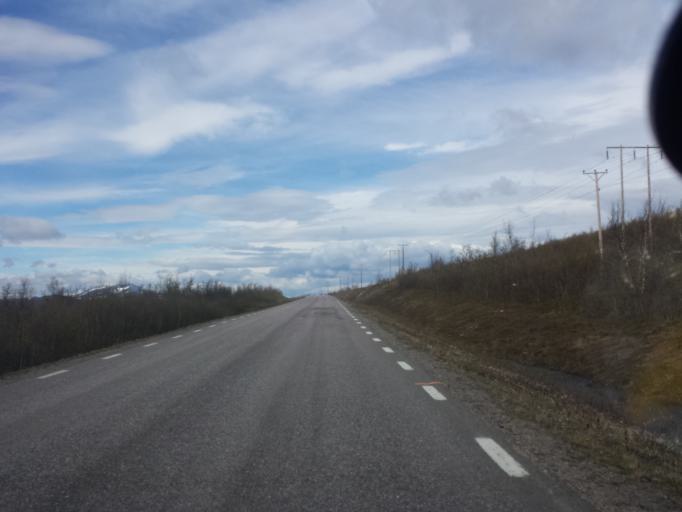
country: SE
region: Norrbotten
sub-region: Kiruna Kommun
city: Kiruna
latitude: 68.0452
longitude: 19.8301
